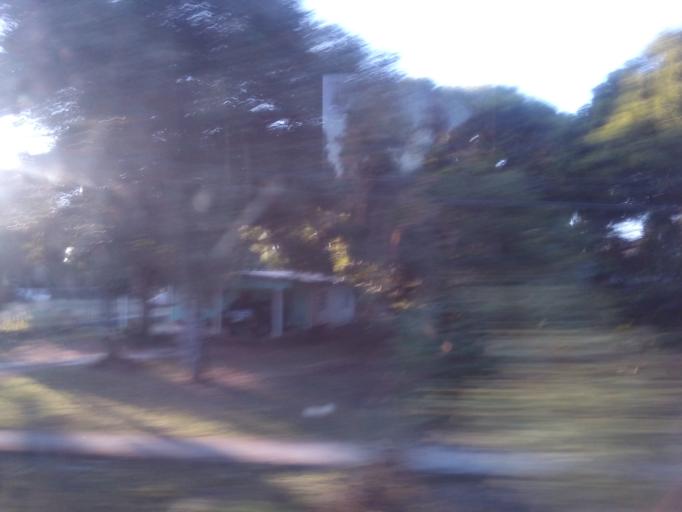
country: PA
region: Veraguas
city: Atalaya
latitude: 8.0800
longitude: -80.8988
